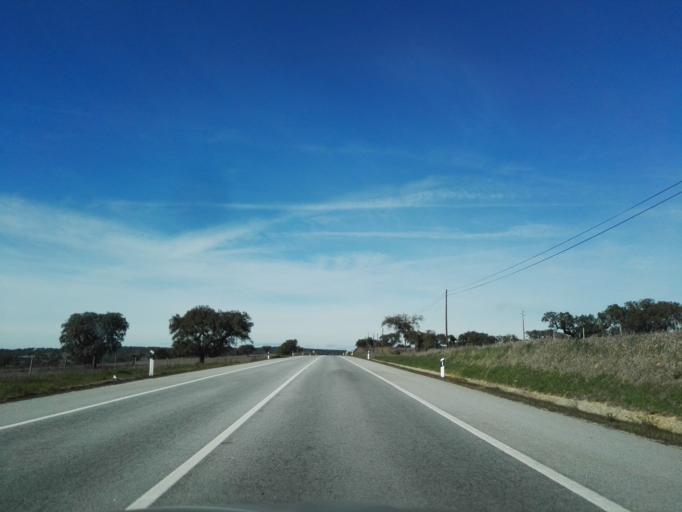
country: PT
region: Portalegre
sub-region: Arronches
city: Arronches
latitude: 39.1497
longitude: -7.3093
